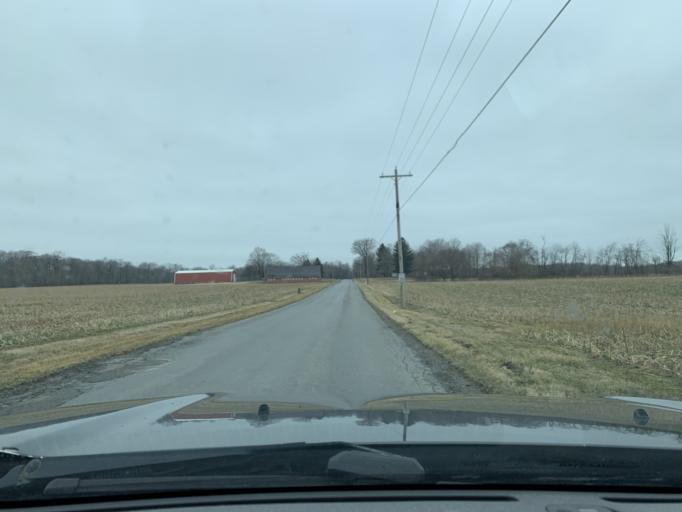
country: US
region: Indiana
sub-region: Porter County
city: Chesterton
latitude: 41.6070
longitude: -86.9913
